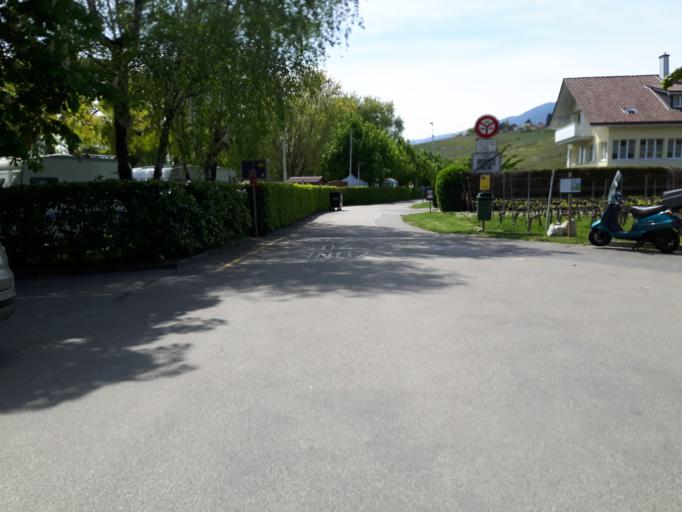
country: CH
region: Neuchatel
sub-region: Boudry District
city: Cortaillod
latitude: 46.9401
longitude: 6.8514
